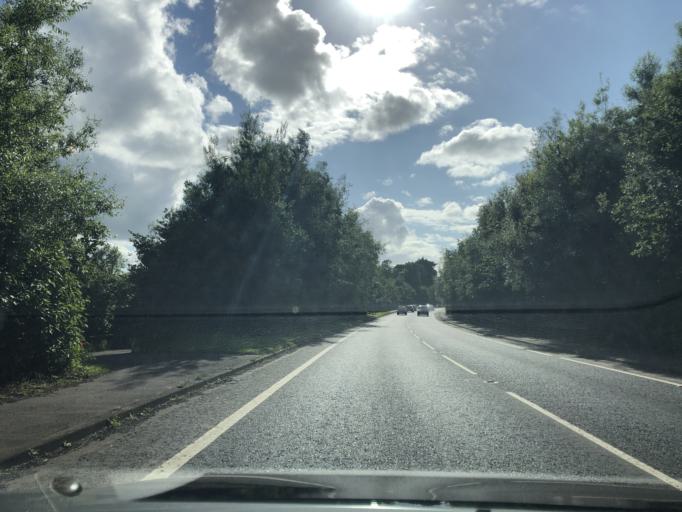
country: GB
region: Northern Ireland
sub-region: Ards District
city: Comber
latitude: 54.5474
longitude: -5.7394
